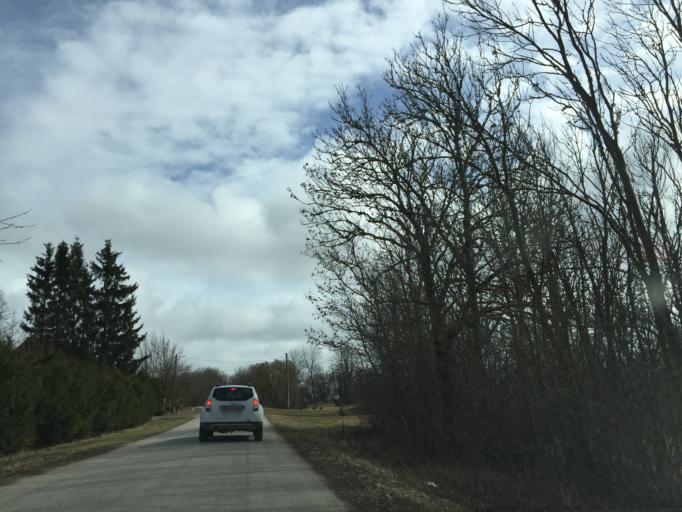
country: EE
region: Laeaene
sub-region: Lihula vald
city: Lihula
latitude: 58.7364
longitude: 23.8361
